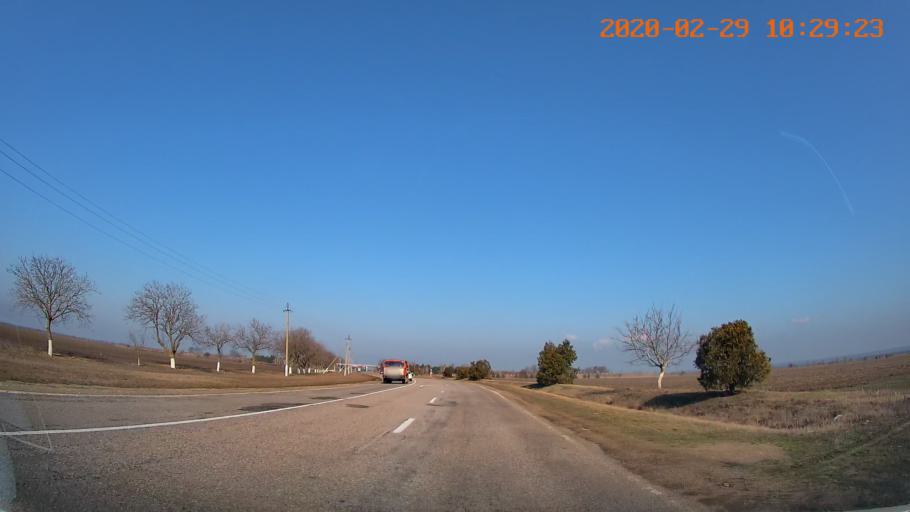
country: MD
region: Telenesti
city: Tiraspolul Nou
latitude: 46.9229
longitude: 29.5860
